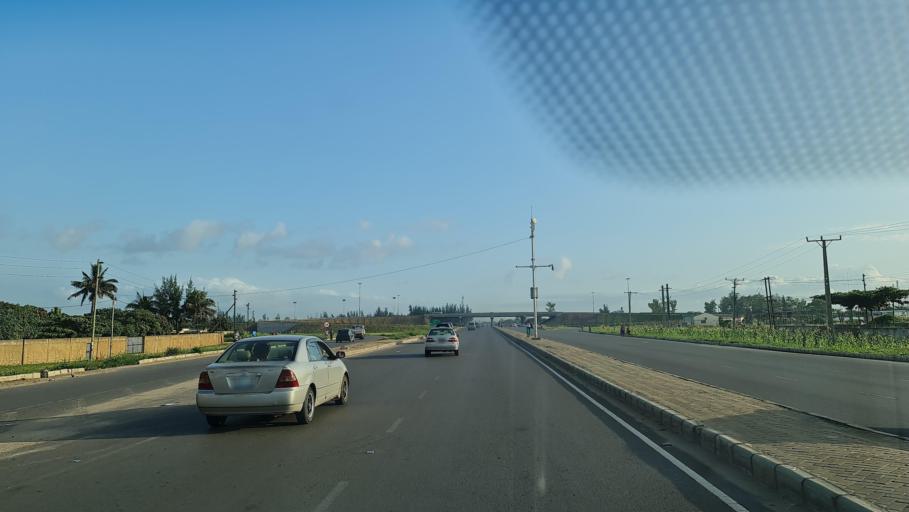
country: MZ
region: Maputo City
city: Maputo
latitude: -25.8209
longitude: 32.5712
